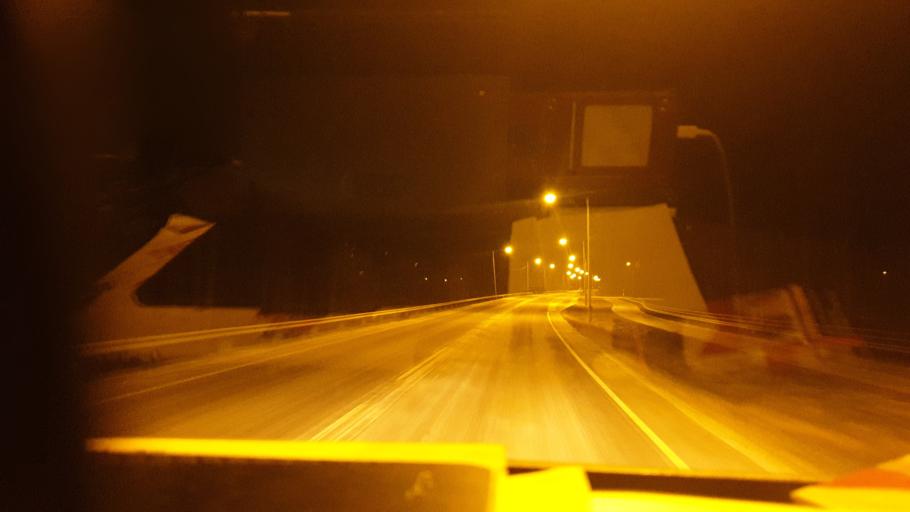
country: FI
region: Southern Ostrobothnia
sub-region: Kuusiokunnat
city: Alavus
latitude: 62.5969
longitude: 23.6587
